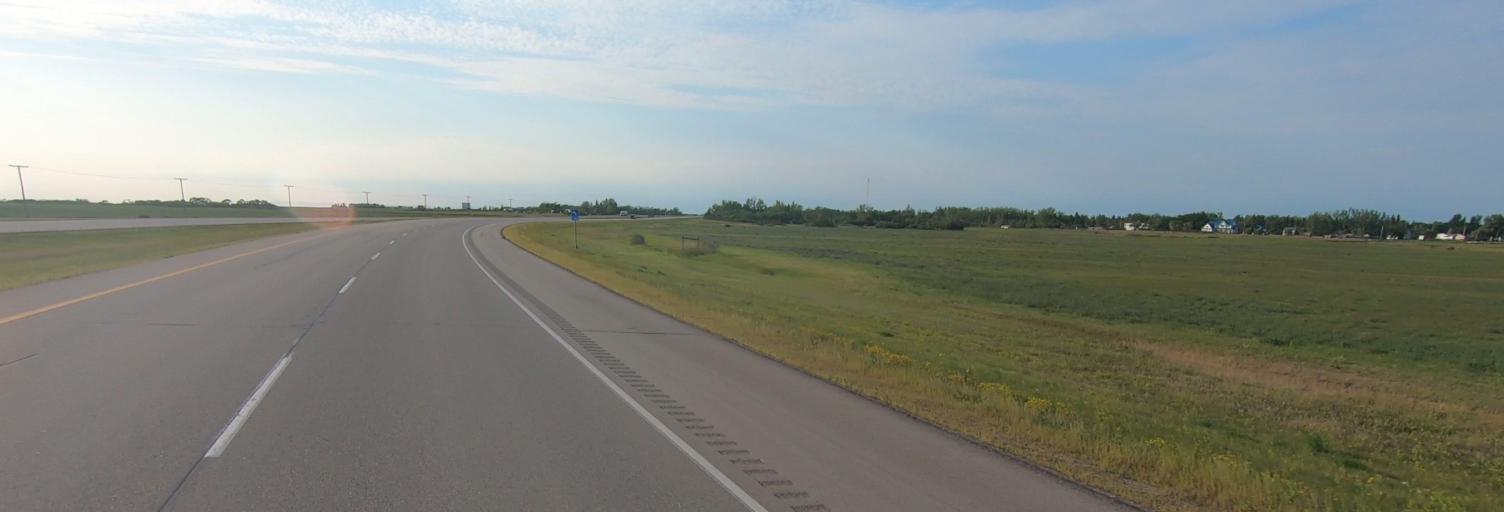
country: CA
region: Saskatchewan
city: Indian Head
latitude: 50.4136
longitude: -103.2765
